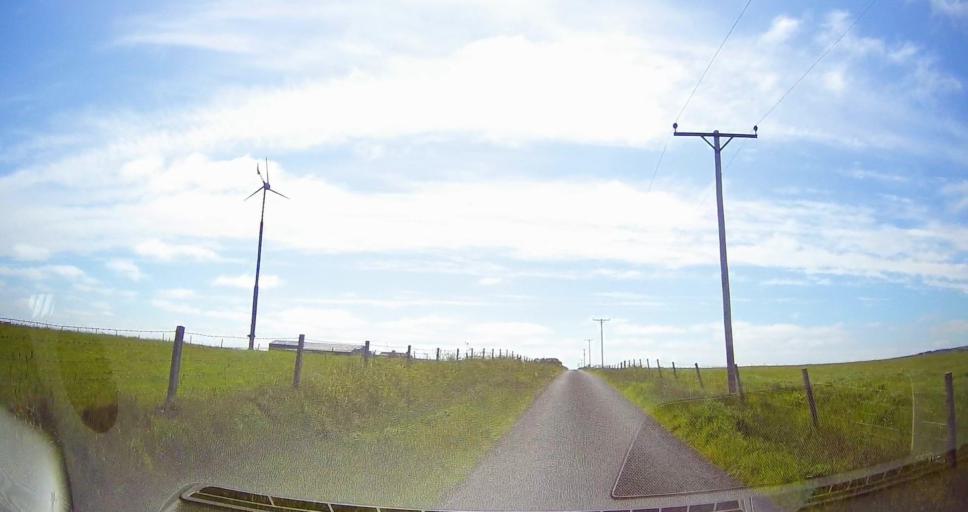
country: GB
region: Scotland
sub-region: Orkney Islands
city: Kirkwall
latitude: 58.8316
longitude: -2.8987
